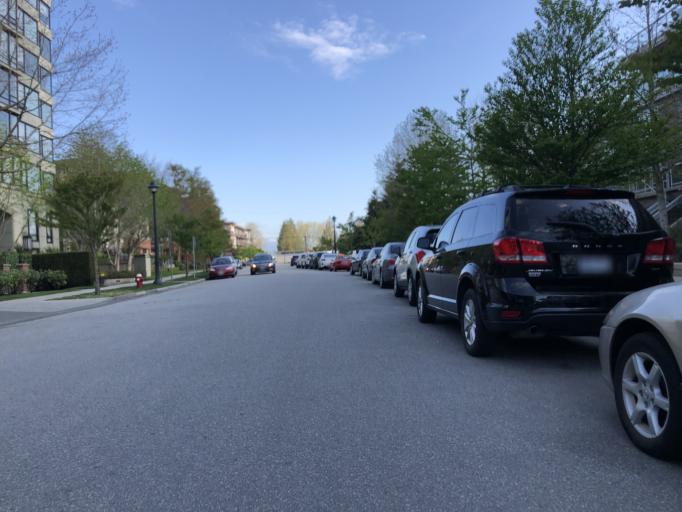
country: CA
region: British Columbia
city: Richmond
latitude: 49.1675
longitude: -123.1220
